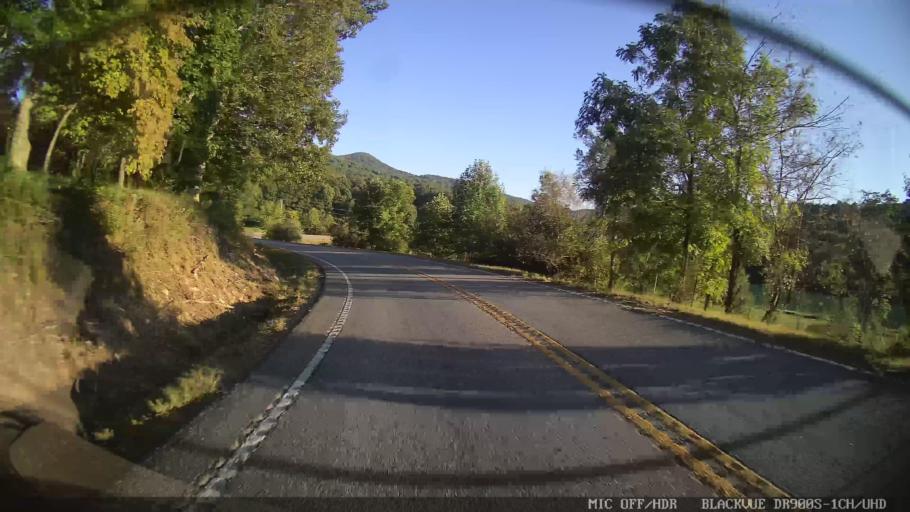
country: US
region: Georgia
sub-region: Fannin County
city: Blue Ridge
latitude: 34.8400
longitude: -84.1925
